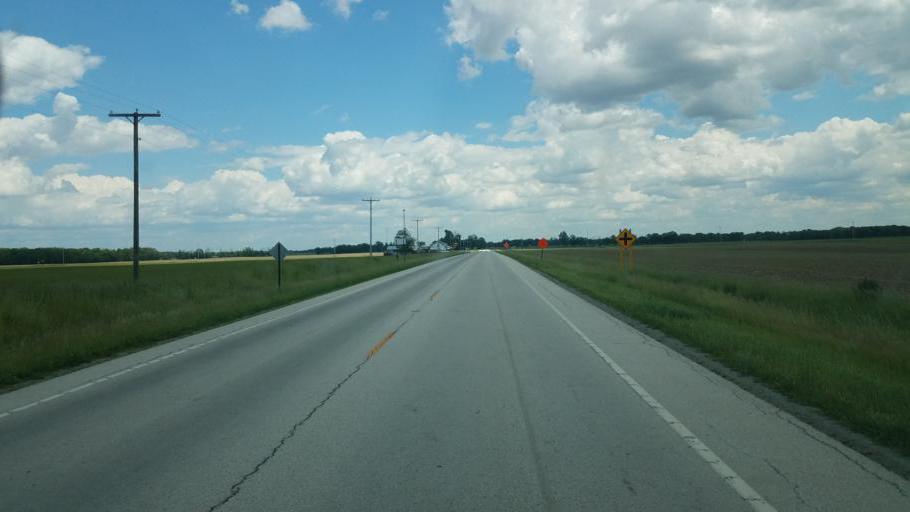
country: US
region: Ohio
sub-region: Wyandot County
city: Upper Sandusky
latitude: 40.8407
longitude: -83.1362
